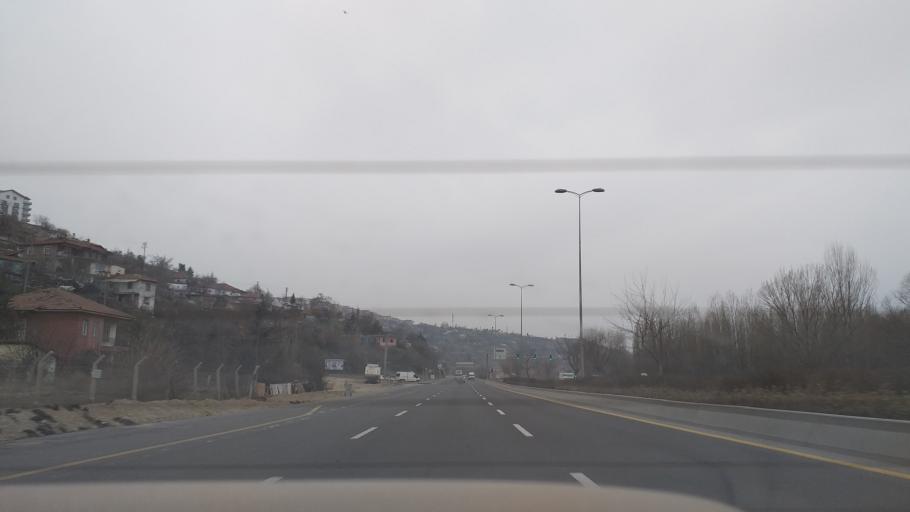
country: TR
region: Ankara
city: Mamak
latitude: 39.9154
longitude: 32.9826
